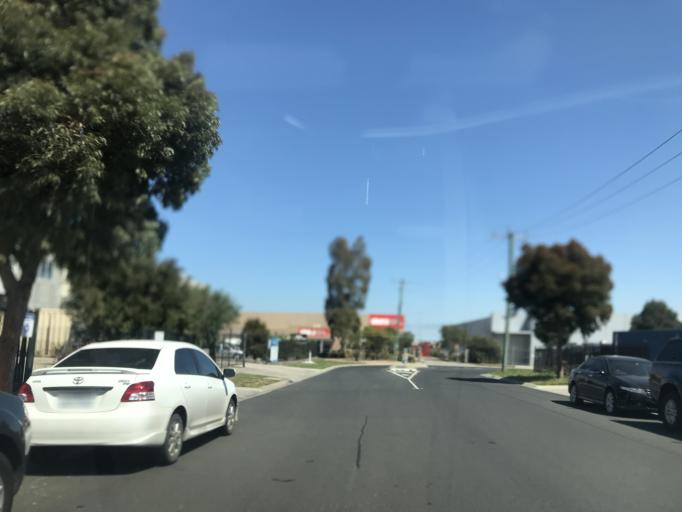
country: AU
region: Victoria
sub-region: Wyndham
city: Truganina
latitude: -37.8243
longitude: 144.7716
